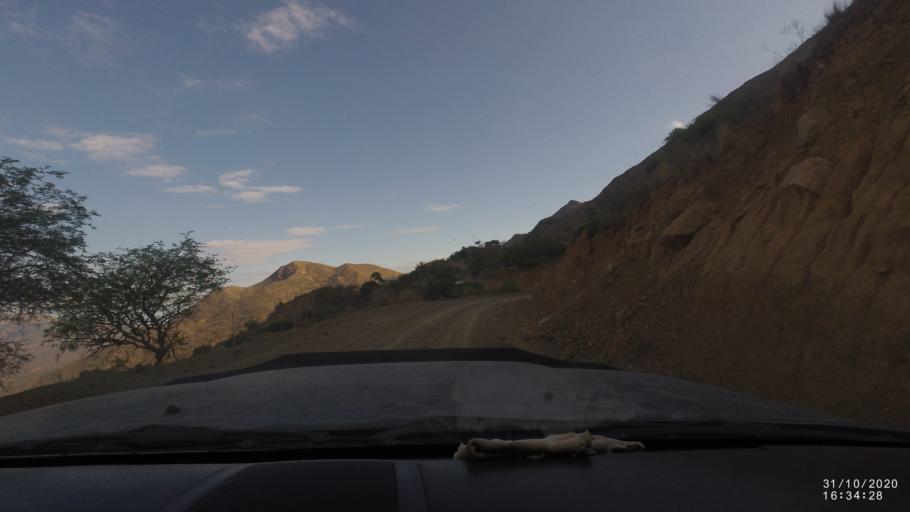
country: BO
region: Chuquisaca
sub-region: Provincia Zudanez
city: Mojocoya
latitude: -18.4486
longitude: -64.5842
